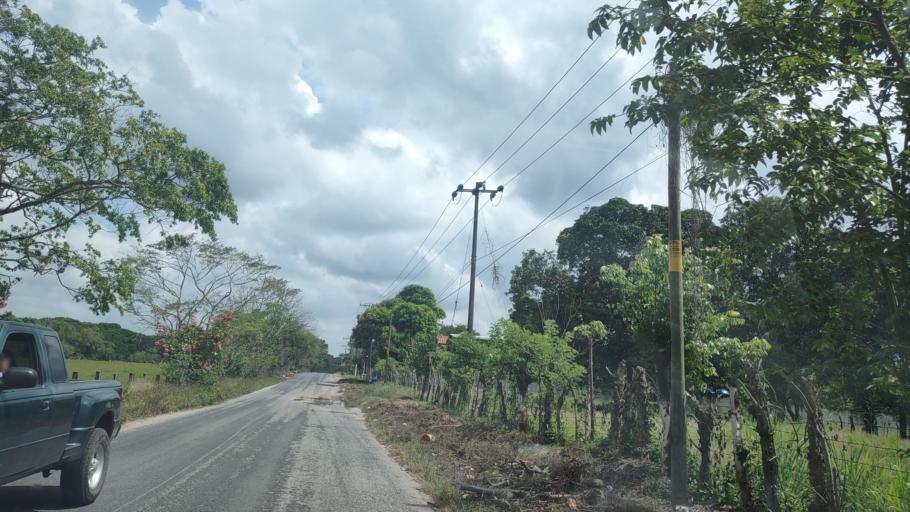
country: MX
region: Veracruz
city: Las Choapas
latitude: 17.9496
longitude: -94.1099
